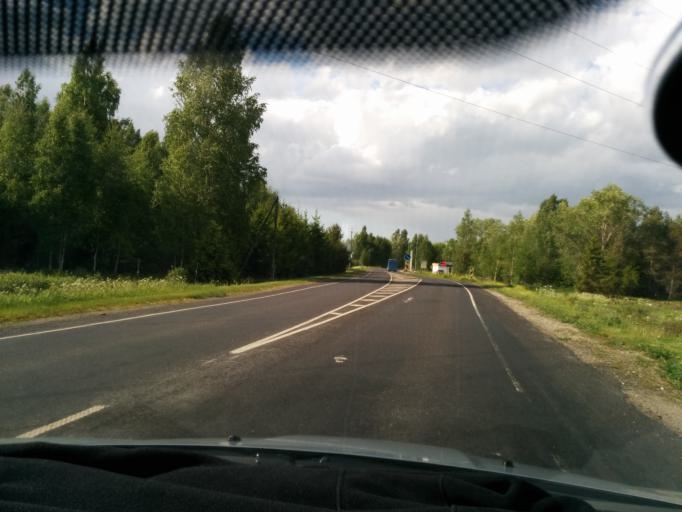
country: EE
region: Harju
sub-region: Loksa linn
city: Loksa
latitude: 59.5678
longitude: 25.7257
